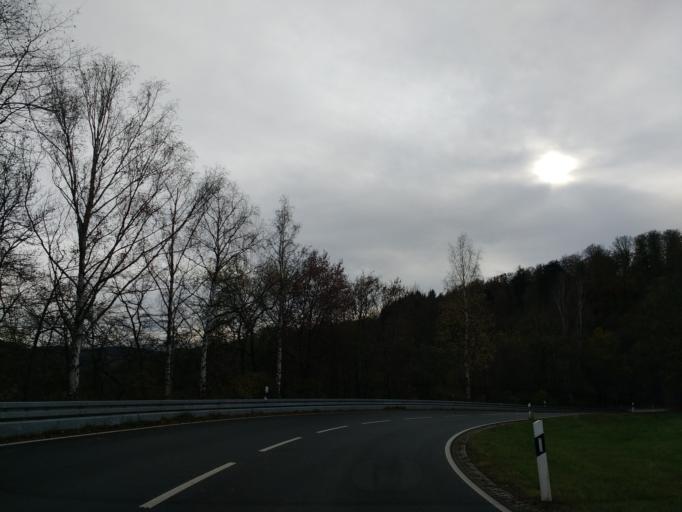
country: DE
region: Hesse
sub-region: Regierungsbezirk Kassel
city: Sachsenhausen
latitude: 51.2117
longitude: 8.9995
